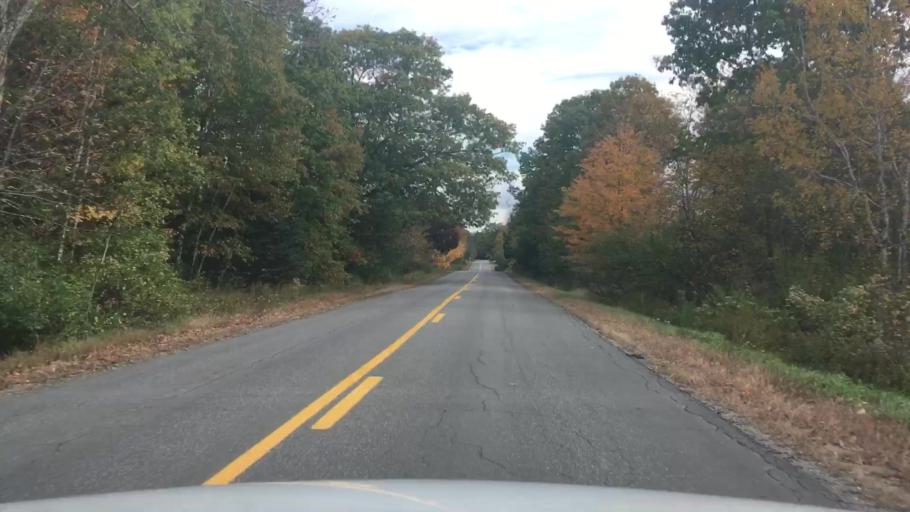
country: US
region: Maine
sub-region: Waldo County
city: Searsmont
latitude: 44.3770
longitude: -69.1378
